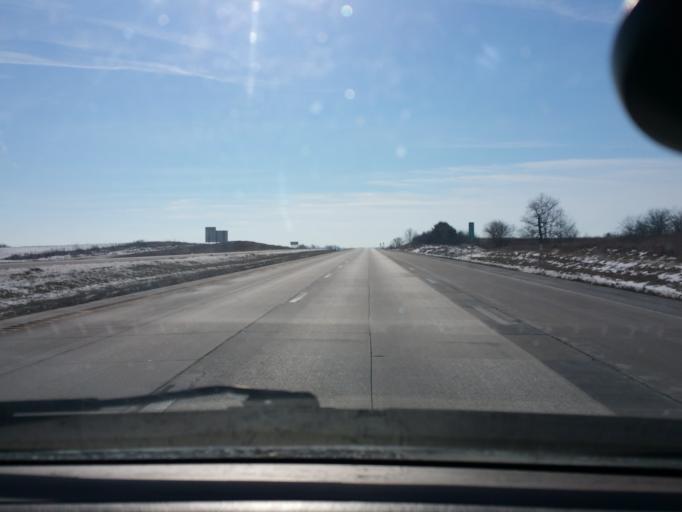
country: US
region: Missouri
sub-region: Harrison County
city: Bethany
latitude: 40.0737
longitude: -94.0937
